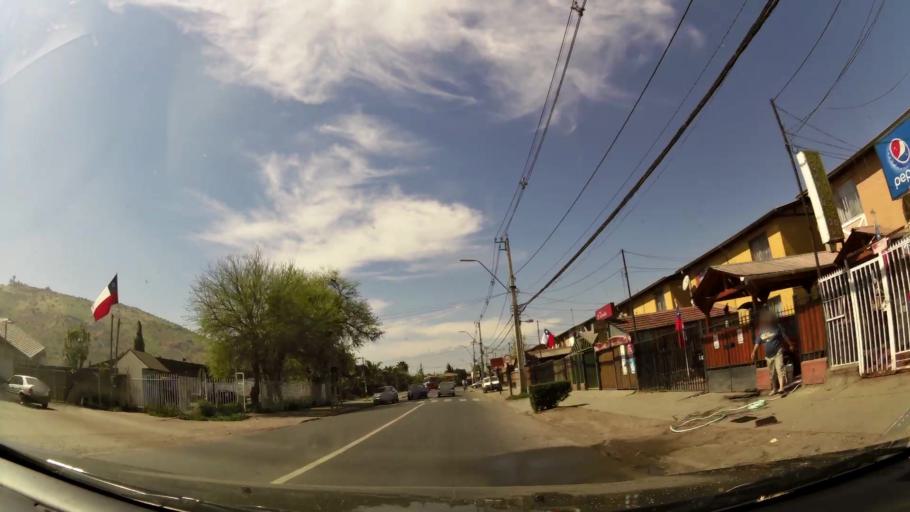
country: CL
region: Santiago Metropolitan
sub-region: Provincia de Santiago
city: Lo Prado
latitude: -33.3985
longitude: -70.7490
